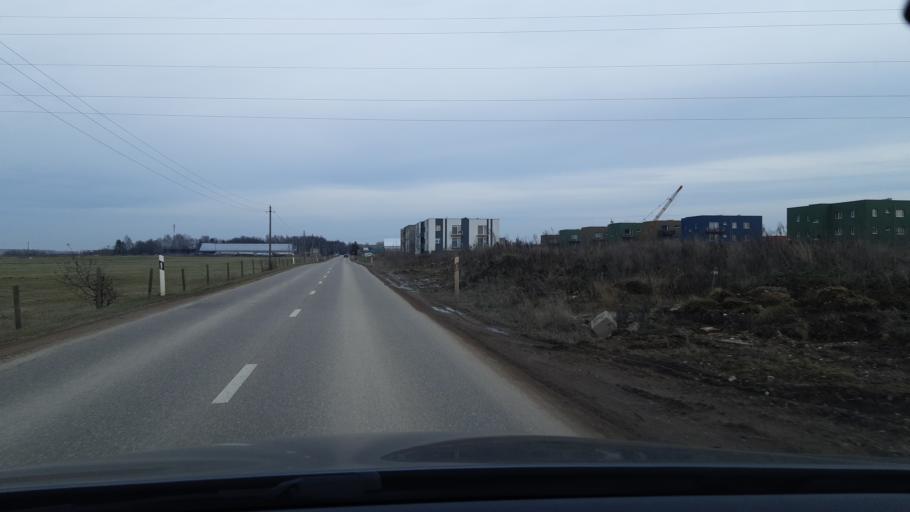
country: LT
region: Kauno apskritis
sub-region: Kaunas
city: Sargenai
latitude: 54.9528
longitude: 23.8525
